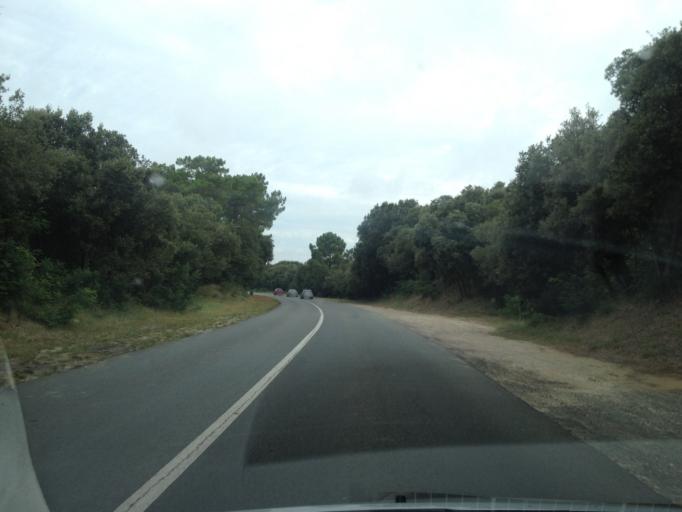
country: FR
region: Poitou-Charentes
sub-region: Departement de la Charente-Maritime
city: Les Mathes
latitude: 45.6740
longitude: -1.1465
